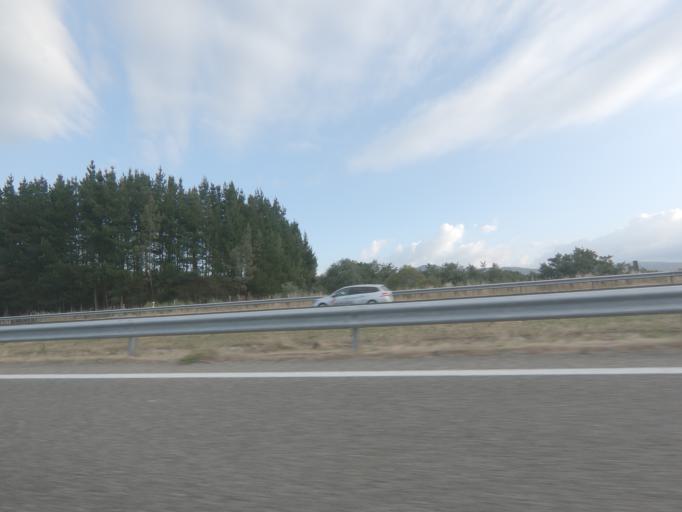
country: ES
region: Galicia
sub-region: Provincia de Ourense
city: Allariz
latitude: 42.2030
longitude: -7.7972
